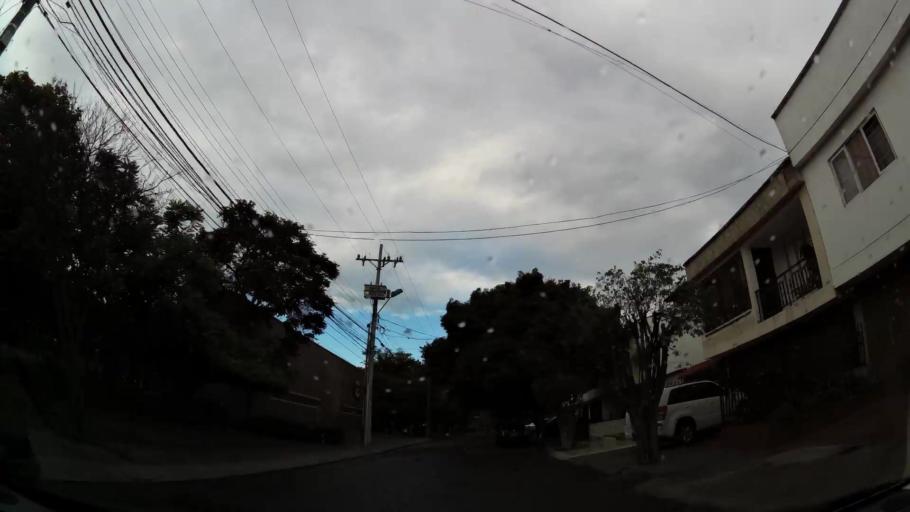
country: CO
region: Valle del Cauca
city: Cali
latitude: 3.4853
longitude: -76.5149
